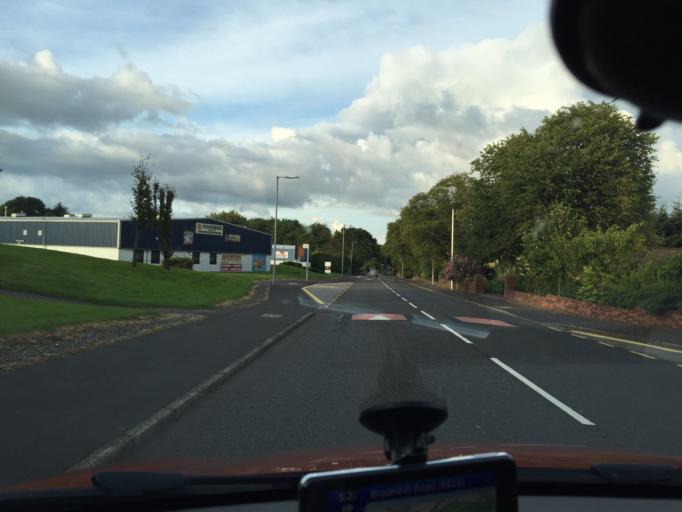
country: GB
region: Scotland
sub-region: North Lanarkshire
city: Cumbernauld
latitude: 55.9758
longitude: -3.9532
